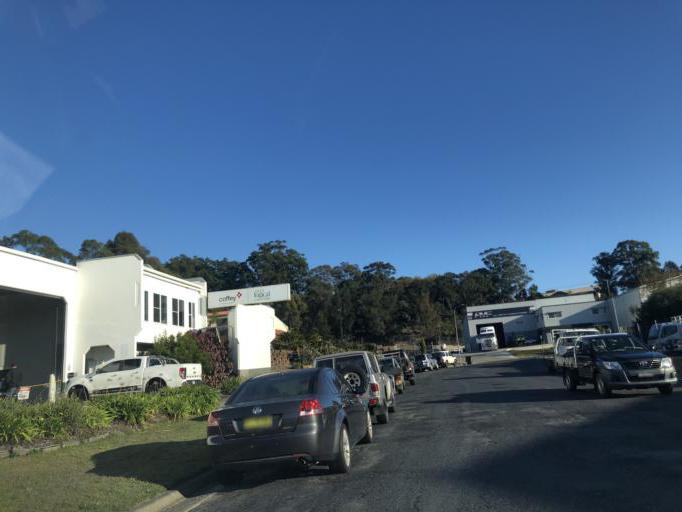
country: AU
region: New South Wales
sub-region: Coffs Harbour
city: Coffs Harbour
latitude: -30.3112
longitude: 153.0999
